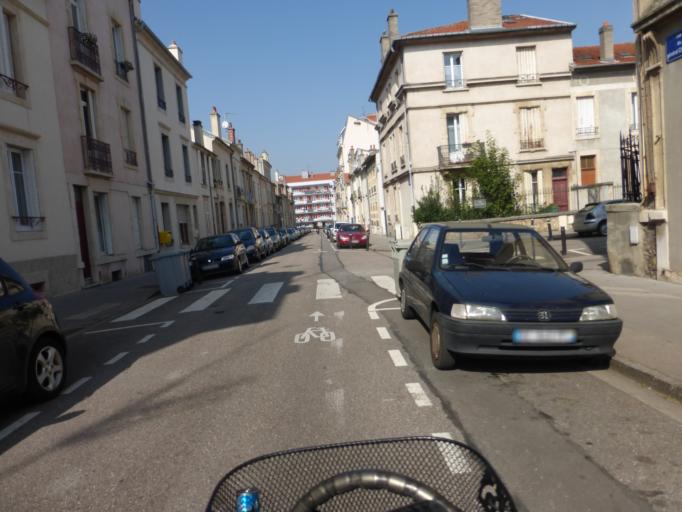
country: FR
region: Lorraine
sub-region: Departement de Meurthe-et-Moselle
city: Villers-les-Nancy
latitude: 48.6751
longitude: 6.1643
